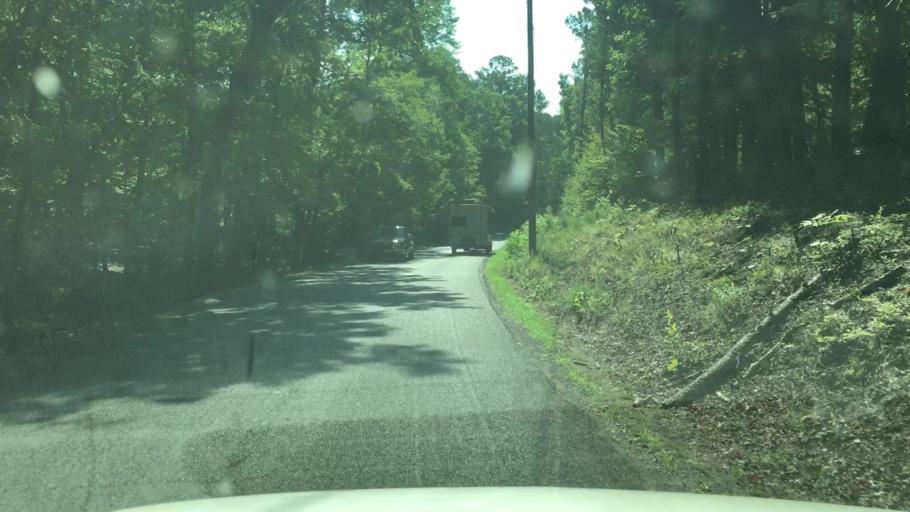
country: US
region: Arkansas
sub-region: Garland County
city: Piney
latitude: 34.5401
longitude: -93.3452
